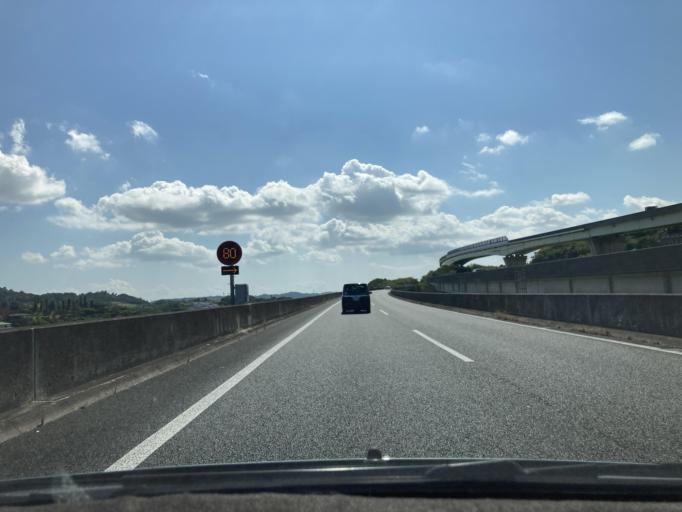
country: JP
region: Okinawa
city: Ginowan
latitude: 26.2206
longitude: 127.7394
